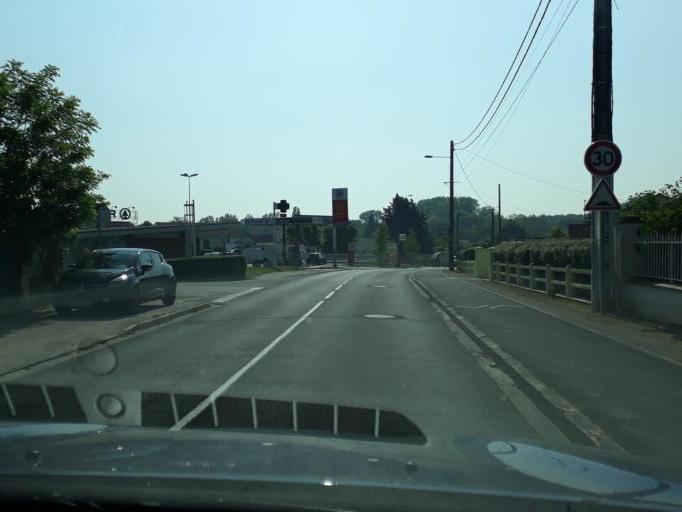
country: FR
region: Centre
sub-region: Departement du Loiret
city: Boigny-sur-Bionne
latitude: 47.9232
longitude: 2.0068
